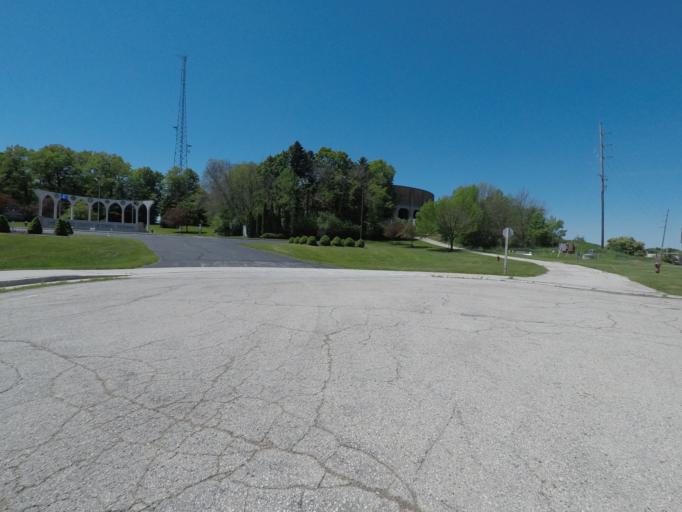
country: US
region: Wisconsin
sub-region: Sheboygan County
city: Sheboygan
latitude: 43.7560
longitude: -87.7488
